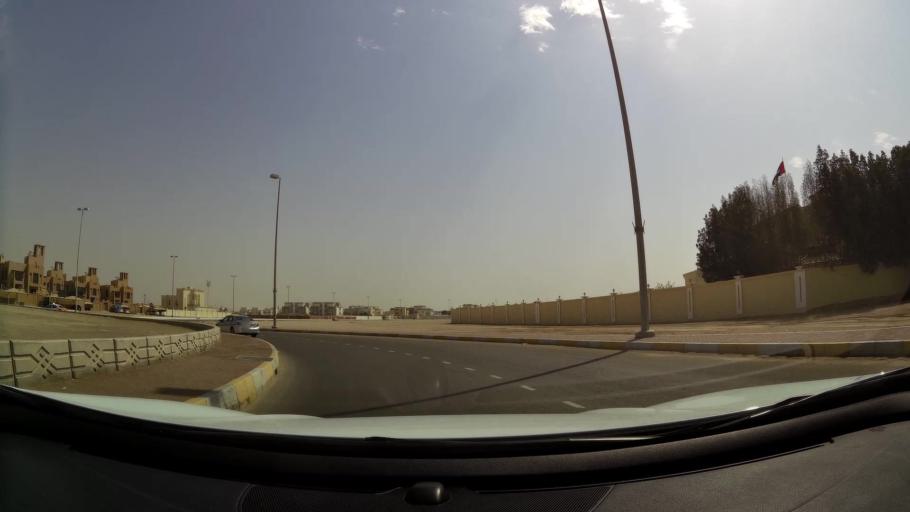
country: AE
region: Abu Dhabi
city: Abu Dhabi
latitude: 24.3362
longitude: 54.5658
